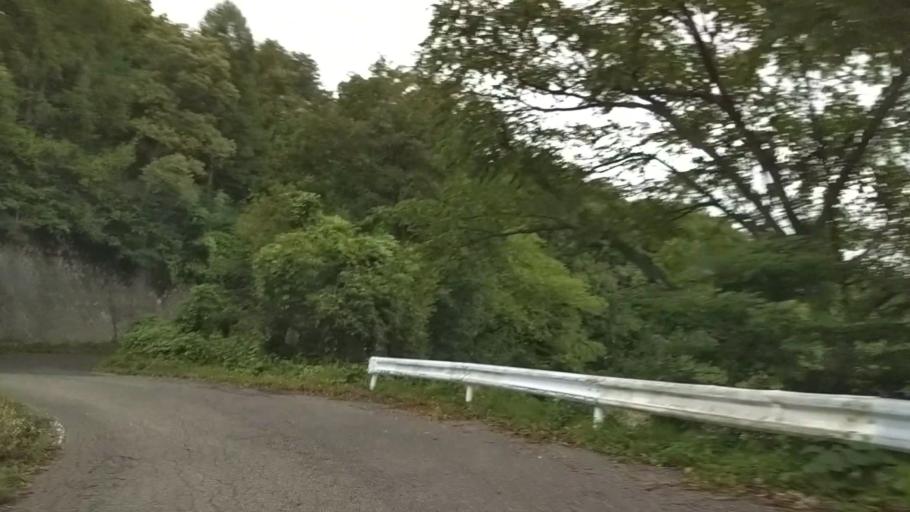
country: JP
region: Nagano
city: Iiyama
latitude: 36.8197
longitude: 138.3894
